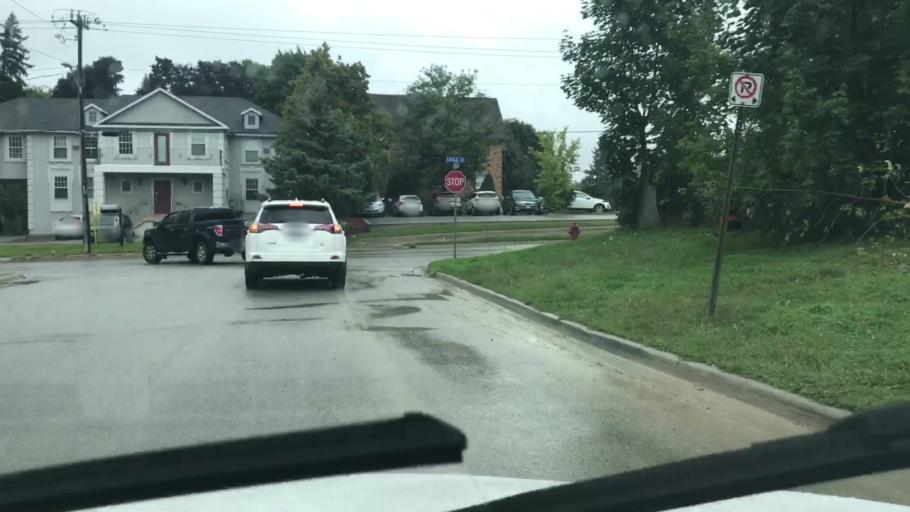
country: CA
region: Ontario
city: Newmarket
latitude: 44.0475
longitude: -79.4675
